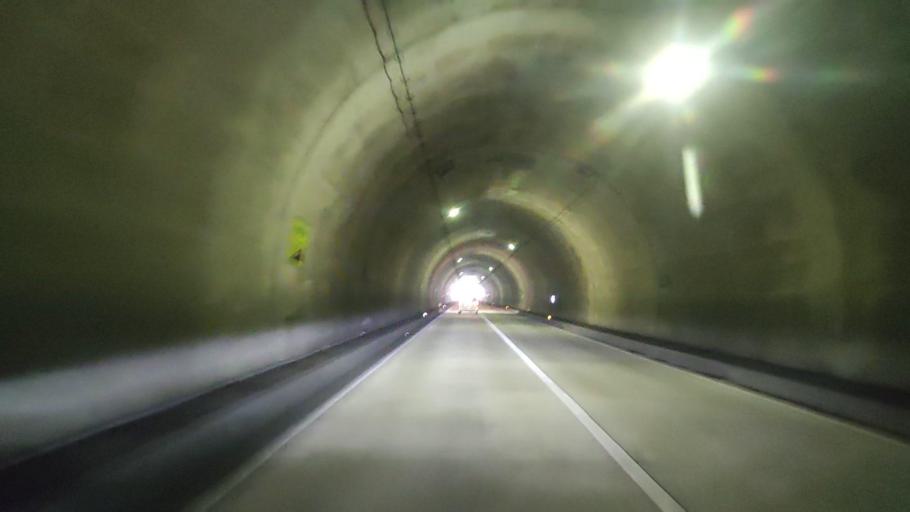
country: JP
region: Nara
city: Yoshino-cho
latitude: 34.2104
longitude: 135.9983
